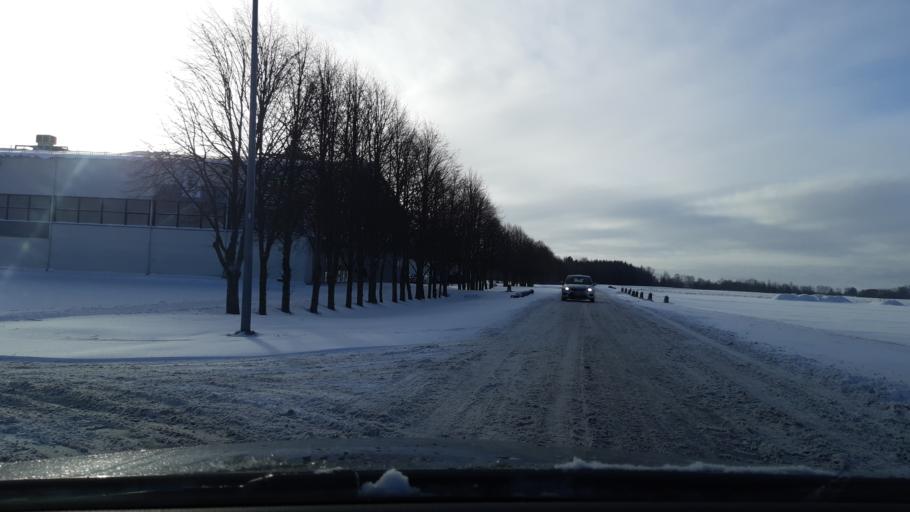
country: LT
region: Kauno apskritis
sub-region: Kauno rajonas
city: Akademija (Kaunas)
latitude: 54.8906
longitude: 23.8313
